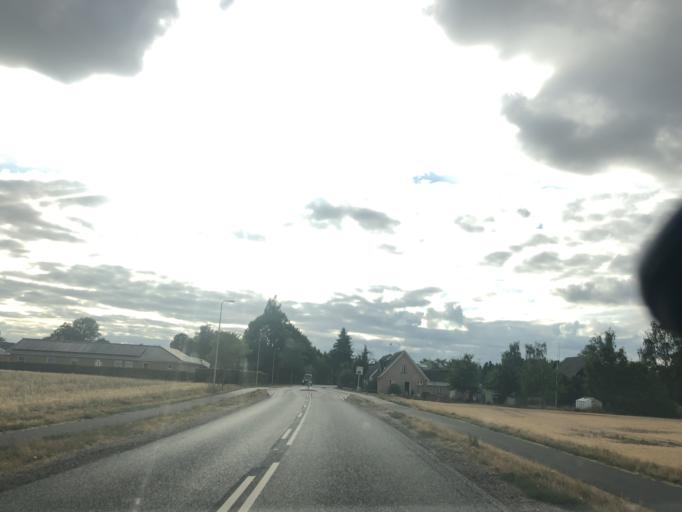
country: DK
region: Zealand
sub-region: Koge Kommune
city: Bjaeverskov
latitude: 55.4276
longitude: 11.9896
